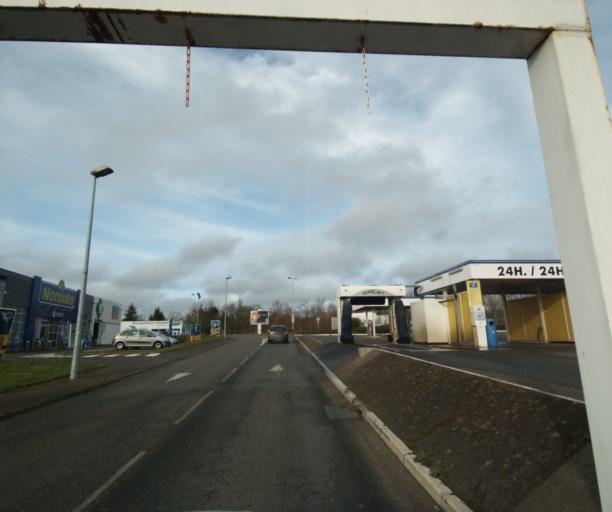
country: FR
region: Pays de la Loire
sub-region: Departement de la Sarthe
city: Allonnes
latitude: 47.9763
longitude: 0.1560
